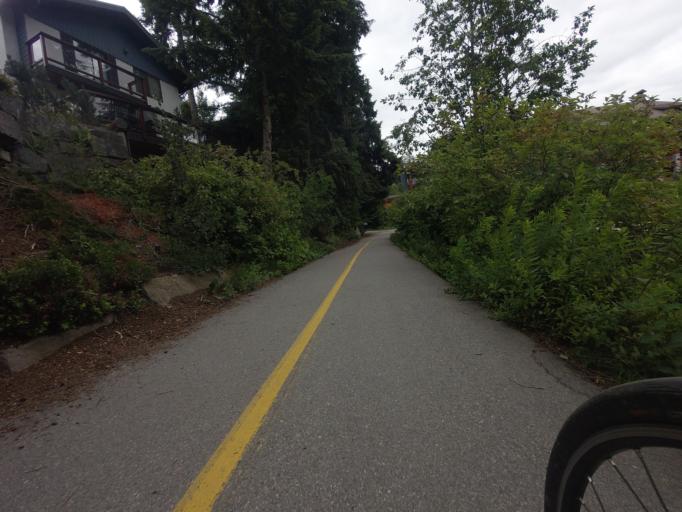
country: CA
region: British Columbia
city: Whistler
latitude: 50.0972
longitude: -122.9947
